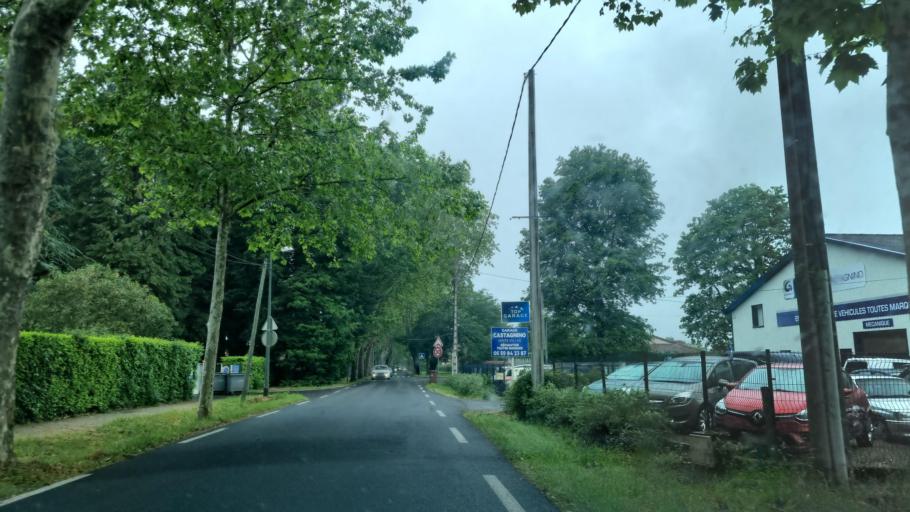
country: FR
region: Aquitaine
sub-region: Departement des Pyrenees-Atlantiques
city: Pau
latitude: 43.3255
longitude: -0.3338
